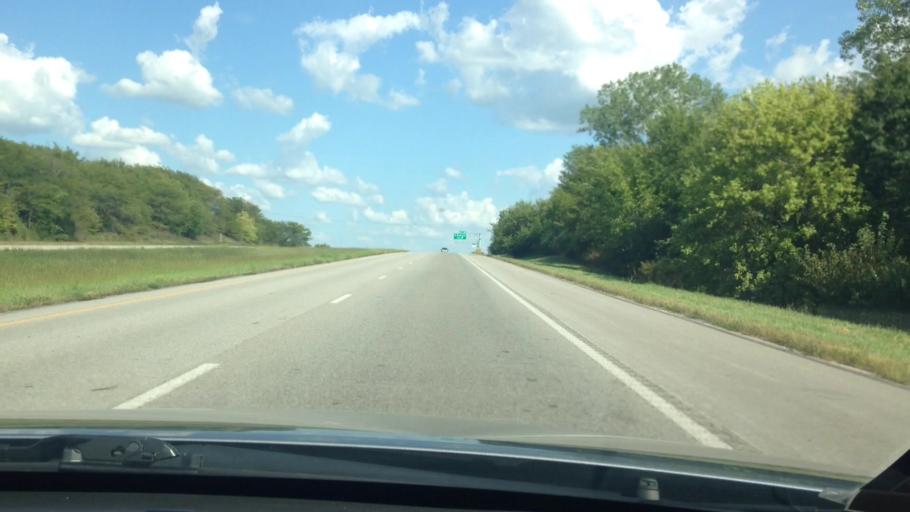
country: US
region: Missouri
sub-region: Clay County
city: Smithville
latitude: 39.3111
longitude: -94.5641
